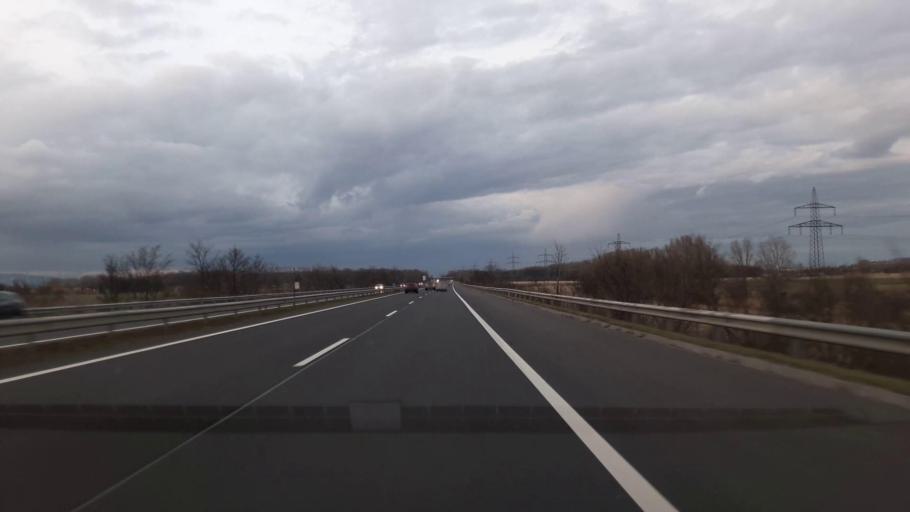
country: AT
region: Burgenland
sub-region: Eisenstadt-Umgebung
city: Hornstein
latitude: 47.8838
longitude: 16.4153
